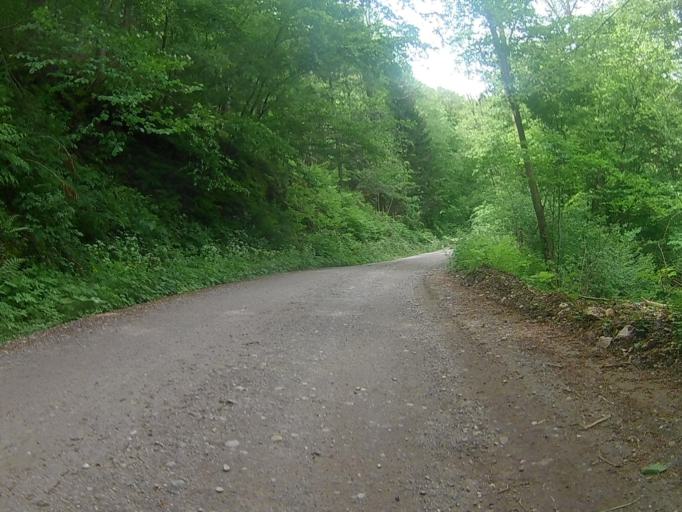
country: SI
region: Race-Fram
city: Morje
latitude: 46.4545
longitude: 15.5775
